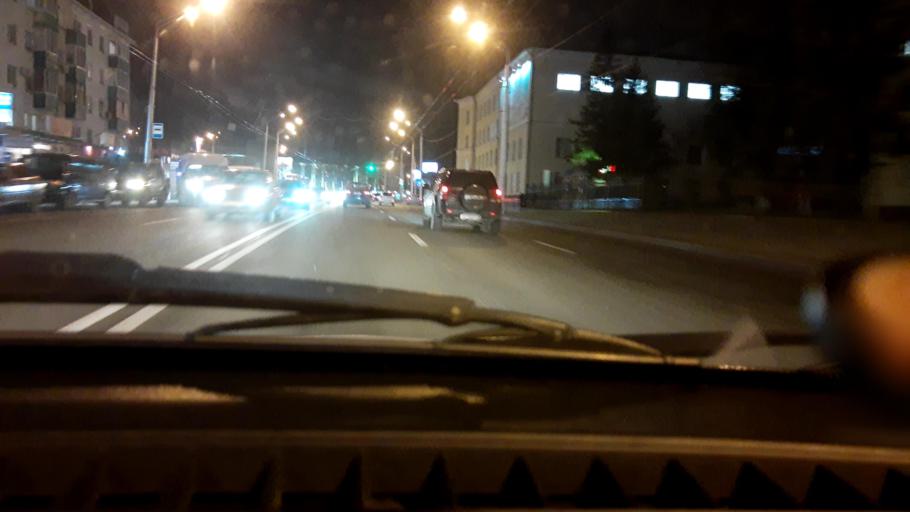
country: RU
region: Bashkortostan
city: Ufa
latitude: 54.7370
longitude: 55.9813
